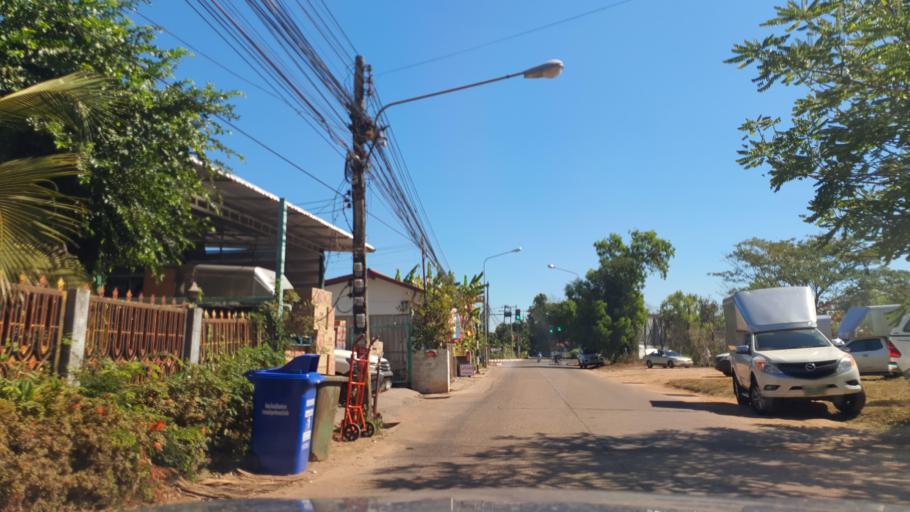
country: TH
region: Sakon Nakhon
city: Sakon Nakhon
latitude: 17.1571
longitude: 104.1251
